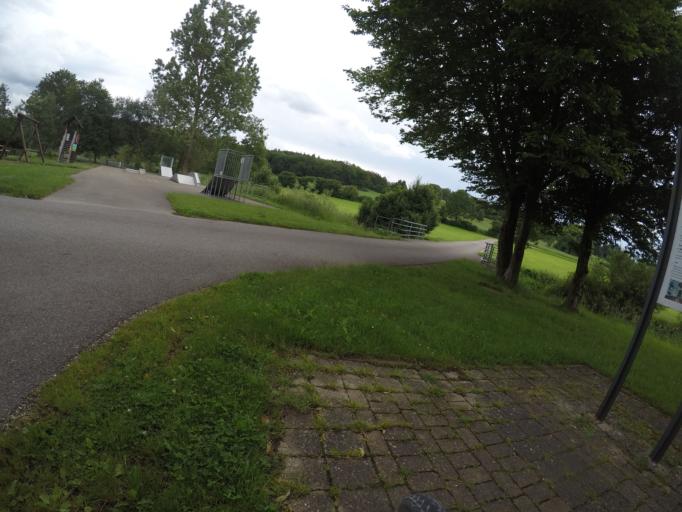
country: DE
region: Baden-Wuerttemberg
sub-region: Tuebingen Region
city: Westerstetten
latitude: 48.5186
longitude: 9.9633
